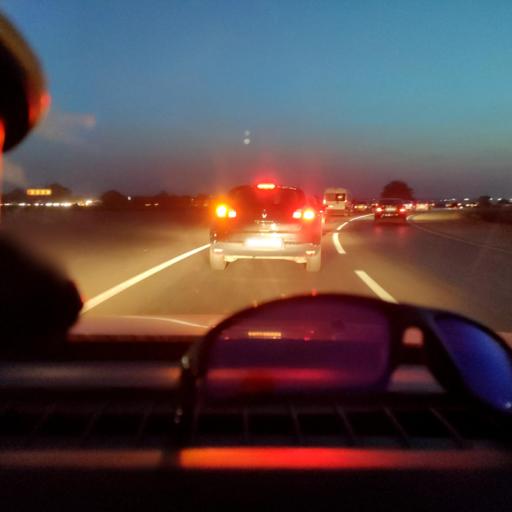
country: RU
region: Samara
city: Samara
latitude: 53.0928
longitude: 50.1526
